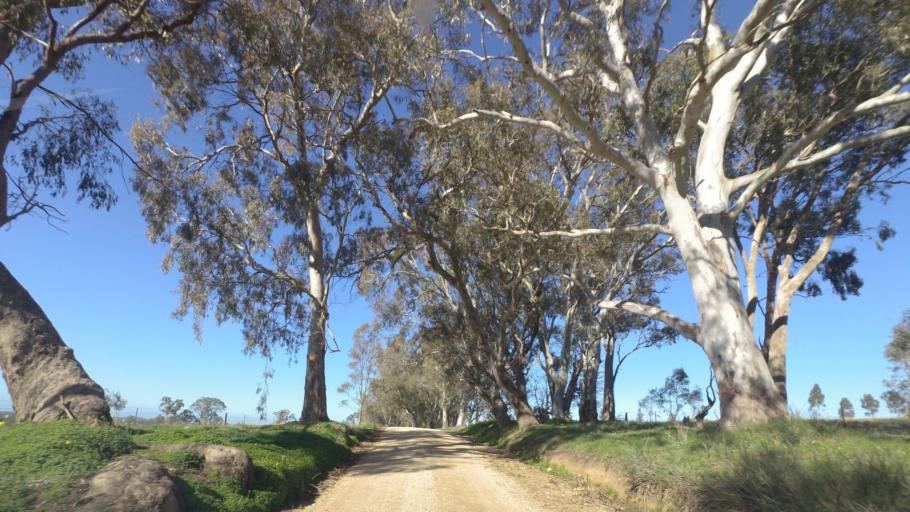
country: AU
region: Victoria
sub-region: Mount Alexander
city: Castlemaine
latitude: -36.9638
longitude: 144.3414
